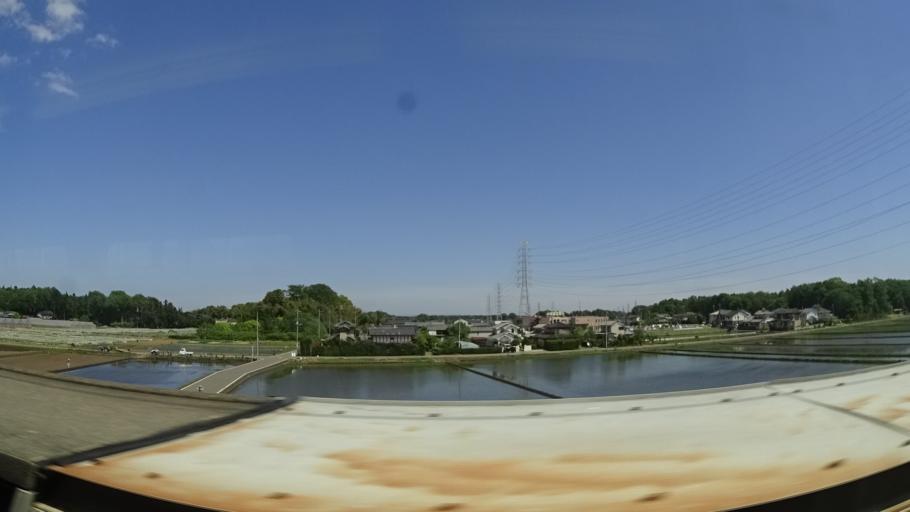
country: JP
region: Tochigi
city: Oyama
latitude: 36.2474
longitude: 139.7656
